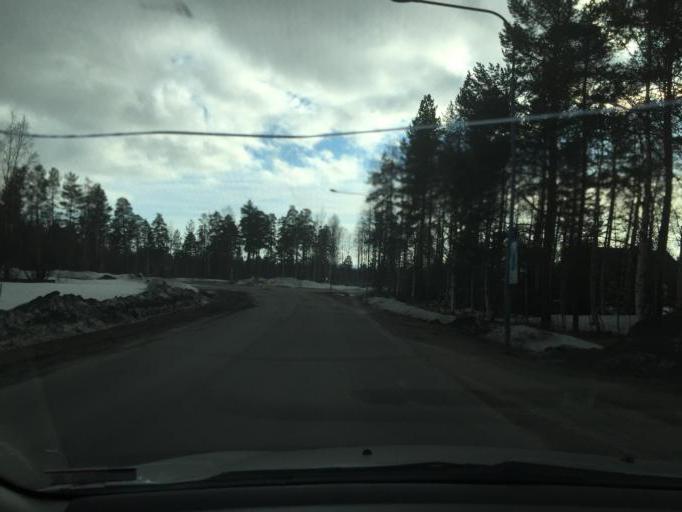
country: SE
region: Norrbotten
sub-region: Lulea Kommun
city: Lulea
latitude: 65.5924
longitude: 22.2263
